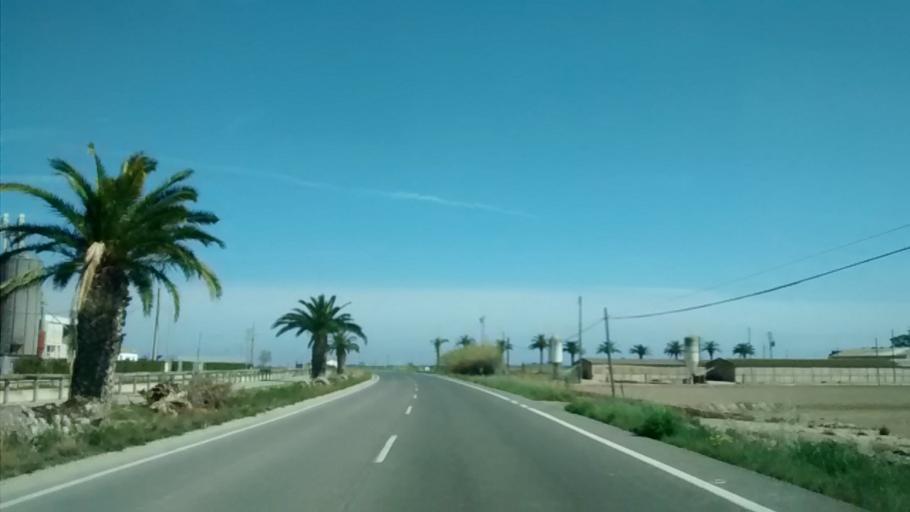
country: ES
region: Catalonia
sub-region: Provincia de Tarragona
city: Deltebre
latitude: 40.7075
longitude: 0.7632
